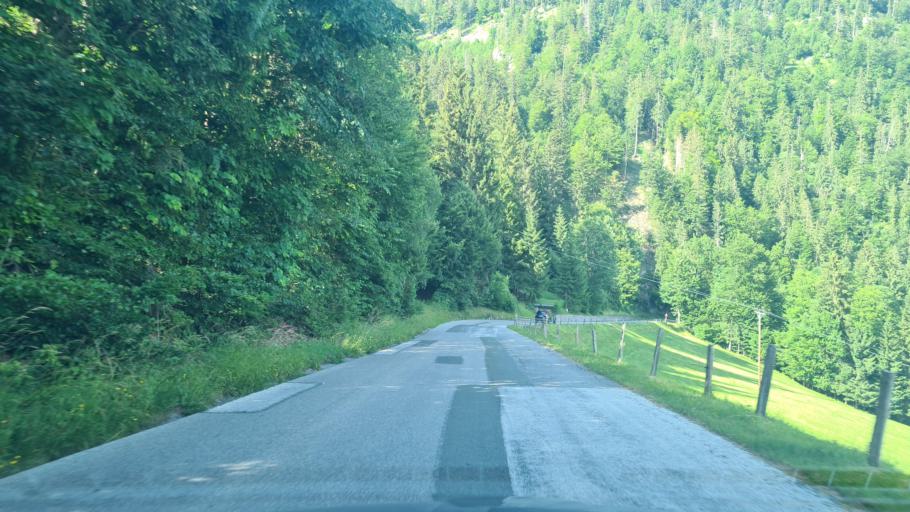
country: AT
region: Salzburg
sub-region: Politischer Bezirk Zell am See
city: Unken
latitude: 47.6511
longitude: 12.6841
